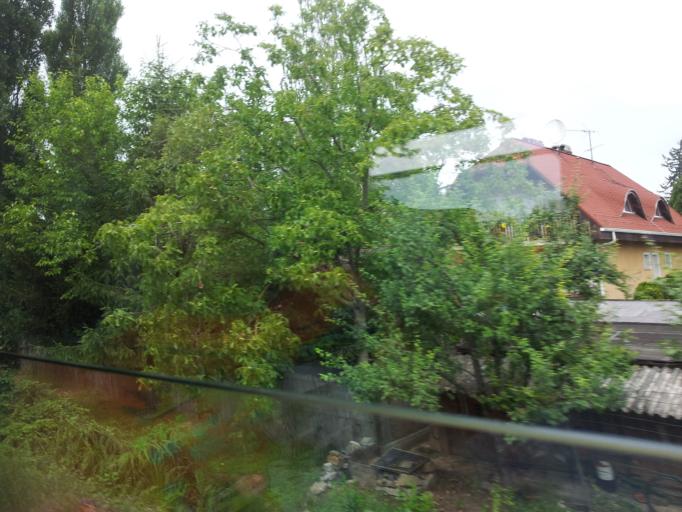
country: HU
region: Veszprem
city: Badacsonytomaj
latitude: 46.7898
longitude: 17.4764
